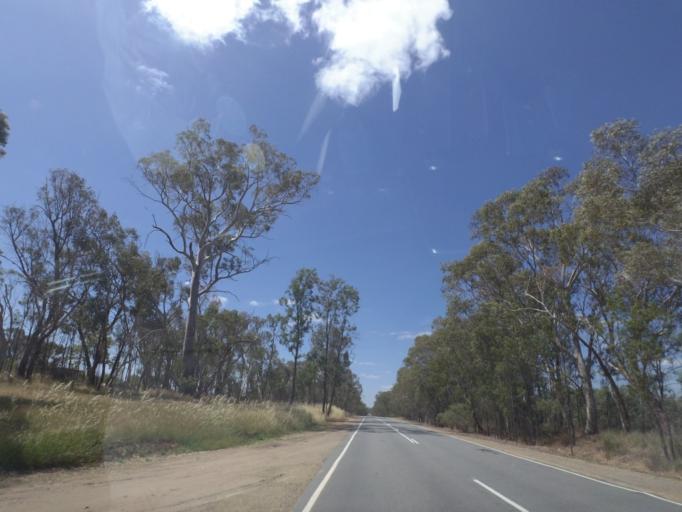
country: AU
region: Victoria
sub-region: Wangaratta
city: Wangaratta
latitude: -36.4443
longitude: 146.2430
